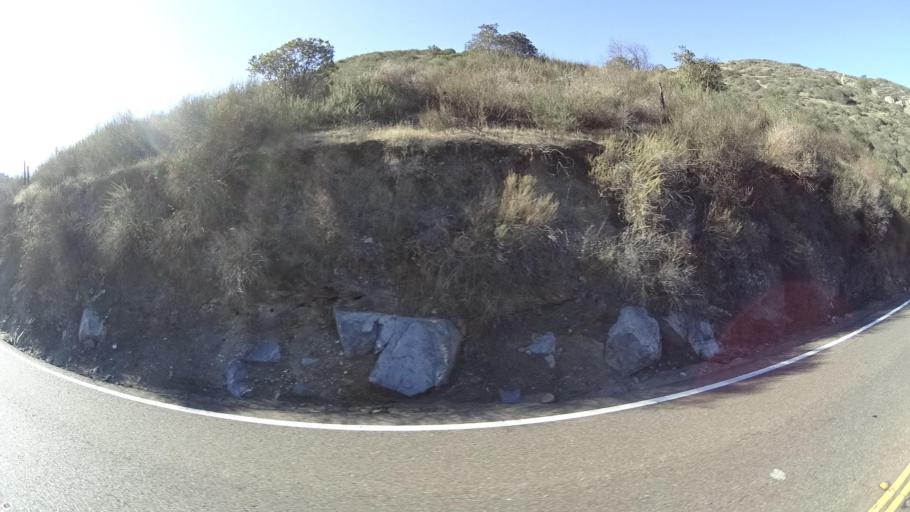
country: US
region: California
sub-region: San Diego County
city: Jamul
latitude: 32.6504
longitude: -116.7874
